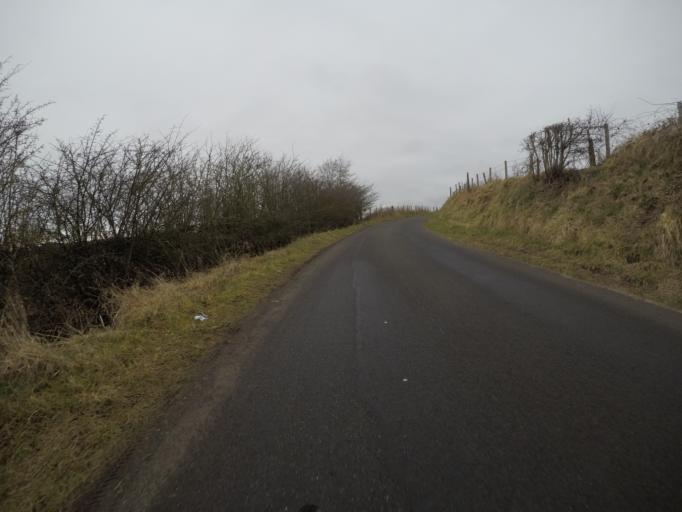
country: GB
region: Scotland
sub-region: North Ayrshire
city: Kilwinning
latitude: 55.6434
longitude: -4.7076
